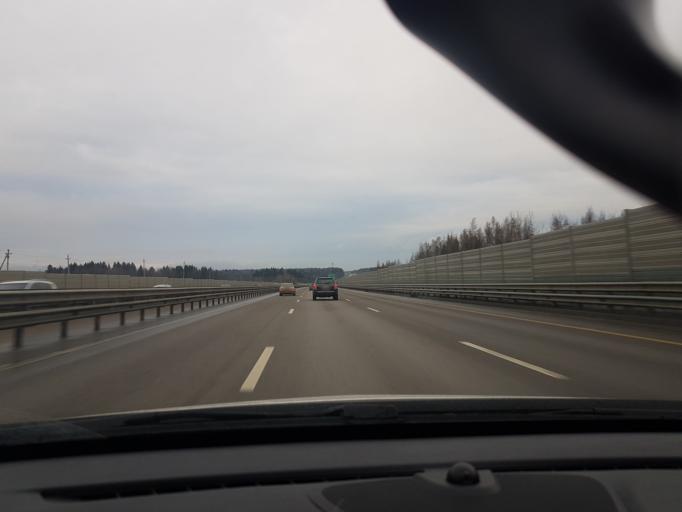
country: RU
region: Moskovskaya
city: Kostrovo
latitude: 55.8800
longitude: 36.6731
